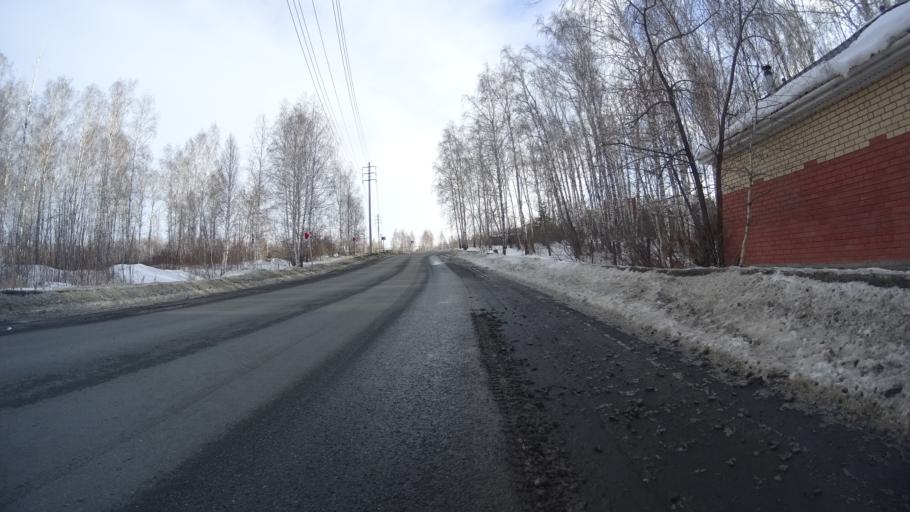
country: RU
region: Chelyabinsk
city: Sargazy
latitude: 55.1291
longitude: 61.2883
